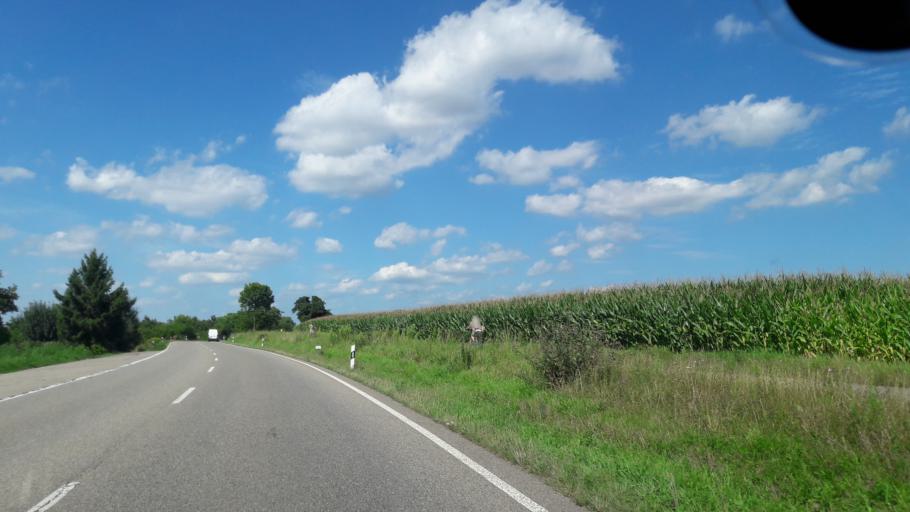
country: DE
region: Baden-Wuerttemberg
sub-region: Karlsruhe Region
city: Kronau
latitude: 49.2345
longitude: 8.6551
